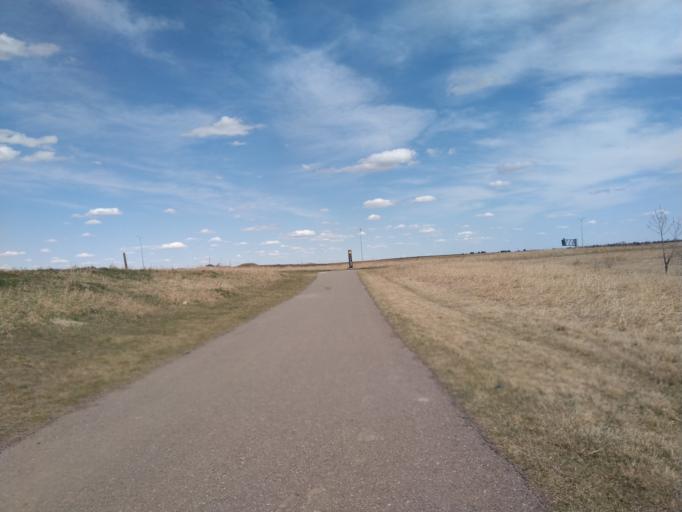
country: CA
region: Alberta
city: Chestermere
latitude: 51.0524
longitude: -113.9243
